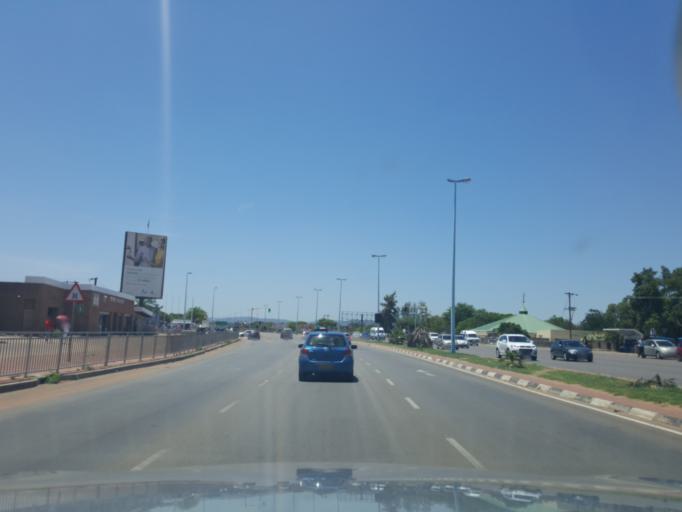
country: BW
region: Kweneng
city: Mogoditshane
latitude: -24.6313
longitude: 25.8734
